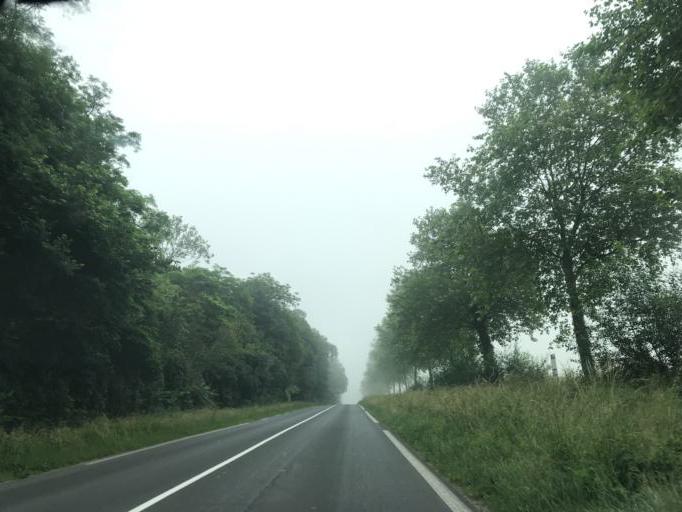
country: FR
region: Ile-de-France
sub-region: Departement de Seine-et-Marne
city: Coupvray
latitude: 48.8829
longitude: 2.7965
